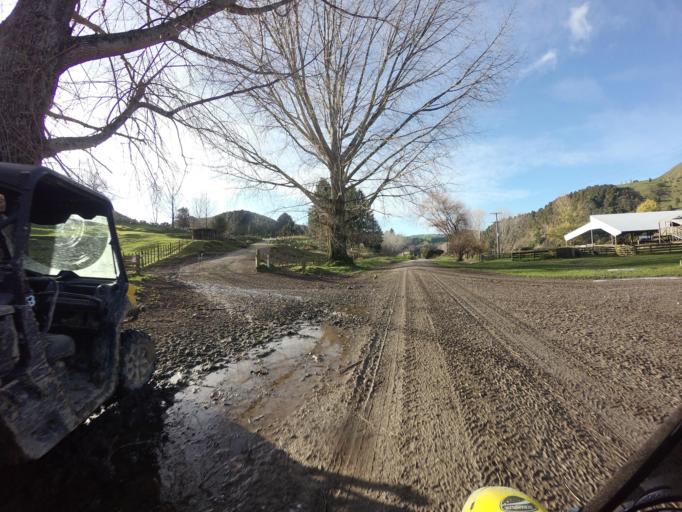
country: NZ
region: Hawke's Bay
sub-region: Wairoa District
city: Wairoa
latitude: -38.7350
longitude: 177.5226
